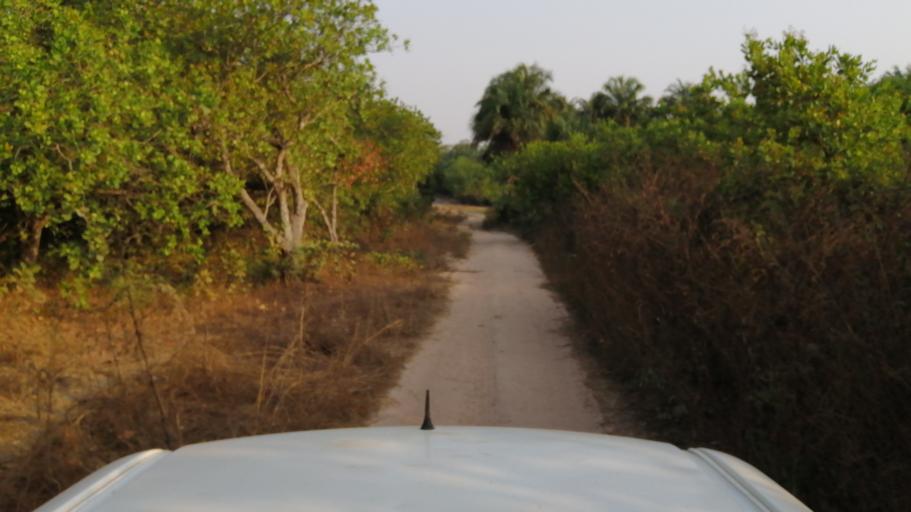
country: GW
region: Oio
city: Mansoa
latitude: 11.9862
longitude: -15.4688
